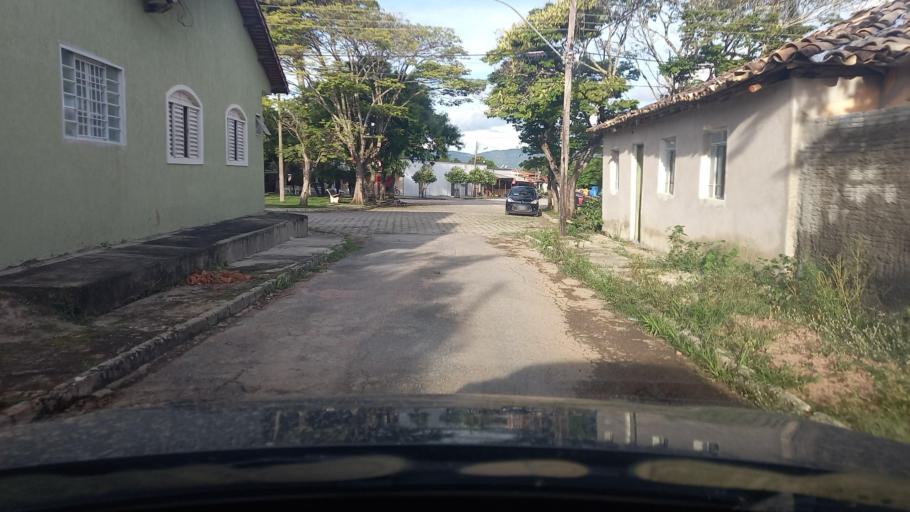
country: BR
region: Goias
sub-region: Cavalcante
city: Cavalcante
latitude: -13.7984
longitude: -47.4608
